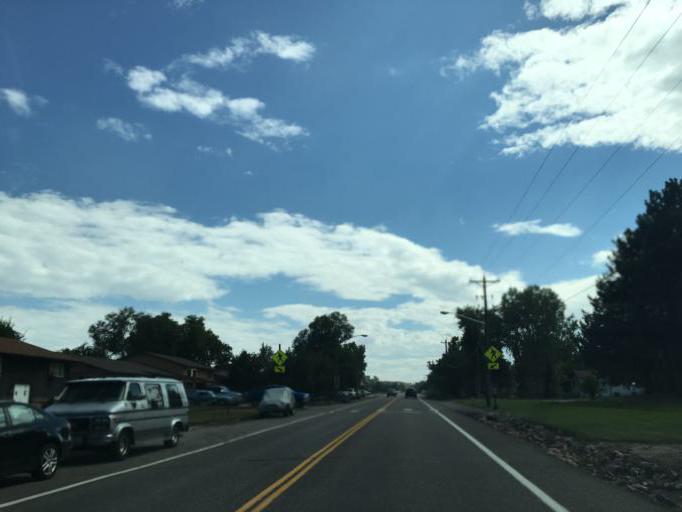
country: US
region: Colorado
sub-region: Jefferson County
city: Applewood
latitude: 39.7526
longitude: -105.1423
